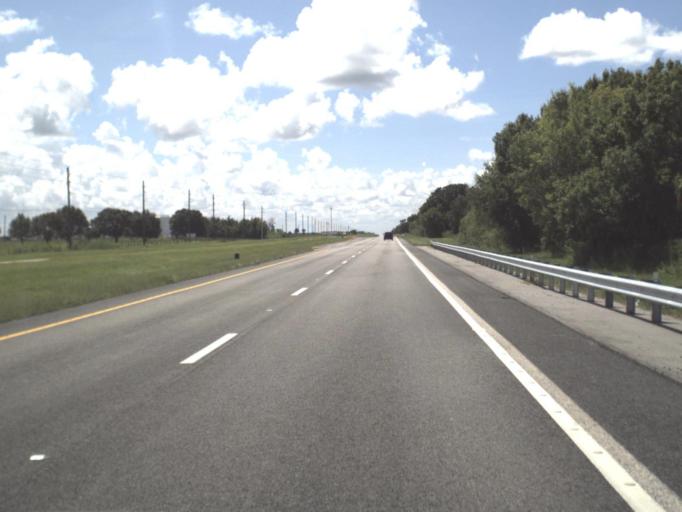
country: US
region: Florida
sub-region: Charlotte County
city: Harbour Heights
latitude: 27.0541
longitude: -81.9585
